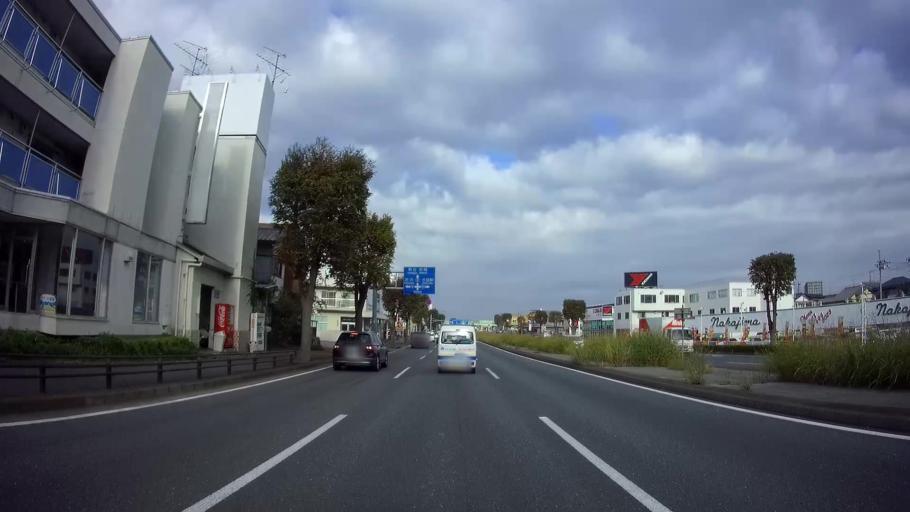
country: JP
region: Saitama
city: Yono
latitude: 35.8970
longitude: 139.6041
